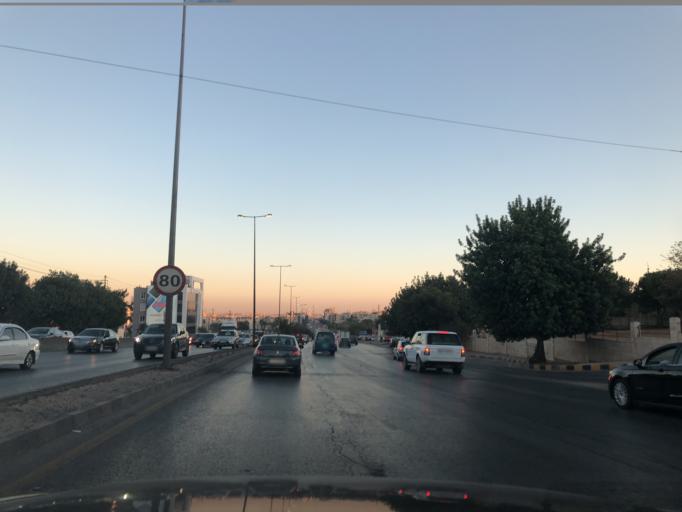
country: JO
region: Amman
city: Wadi as Sir
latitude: 31.9789
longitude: 35.8367
